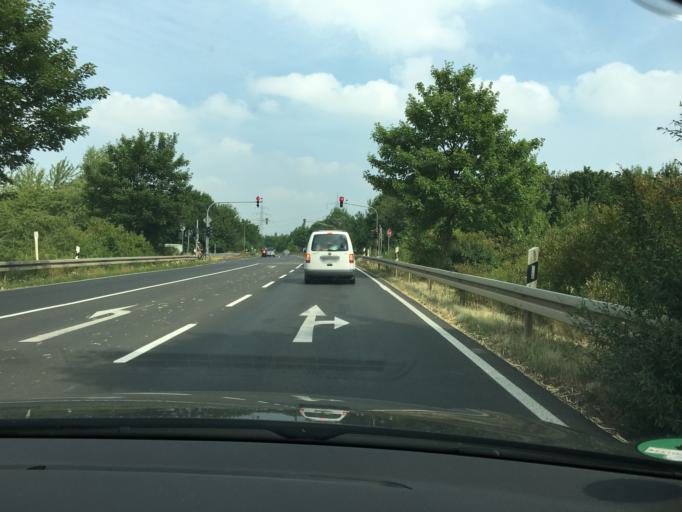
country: DE
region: North Rhine-Westphalia
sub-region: Regierungsbezirk Koln
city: Bergheim
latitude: 50.9359
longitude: 6.6139
